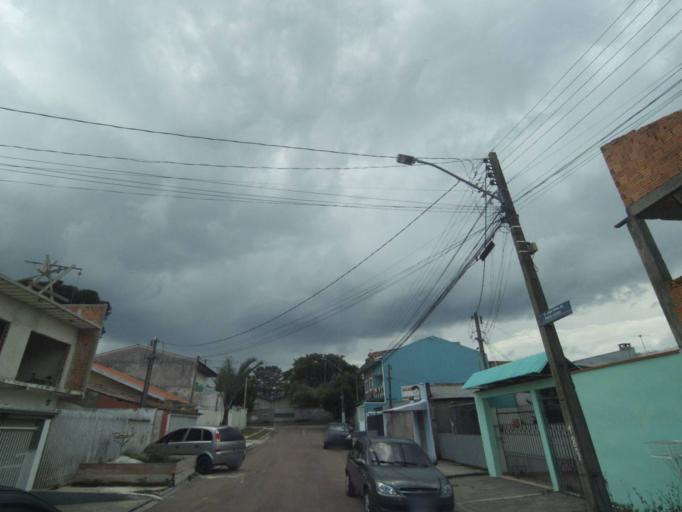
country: BR
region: Parana
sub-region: Curitiba
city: Curitiba
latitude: -25.4658
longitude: -49.3420
